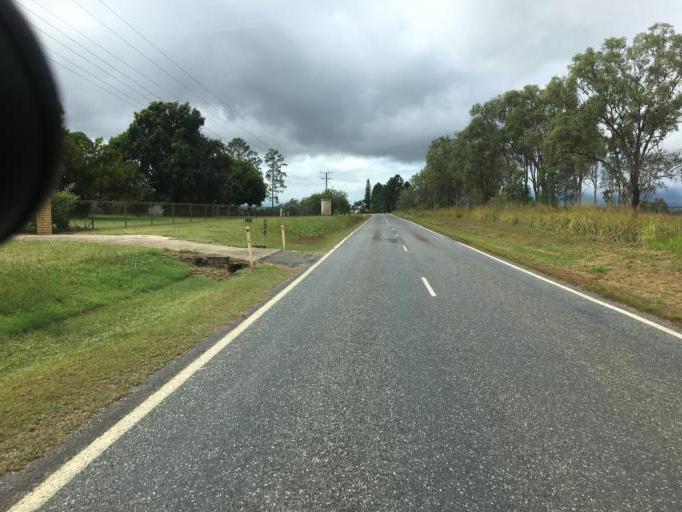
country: AU
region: Queensland
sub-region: Tablelands
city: Mareeba
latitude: -17.0156
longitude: 145.3596
